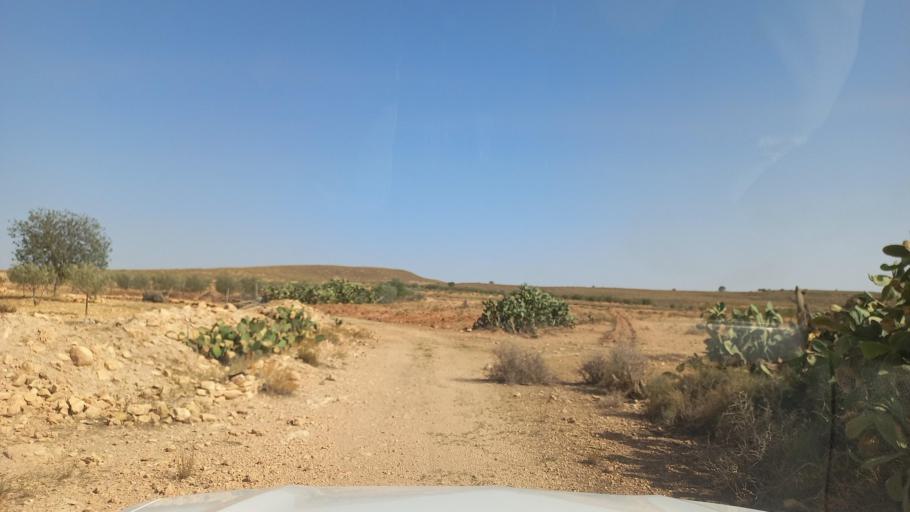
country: TN
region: Al Qasrayn
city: Kasserine
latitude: 35.2057
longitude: 8.9745
